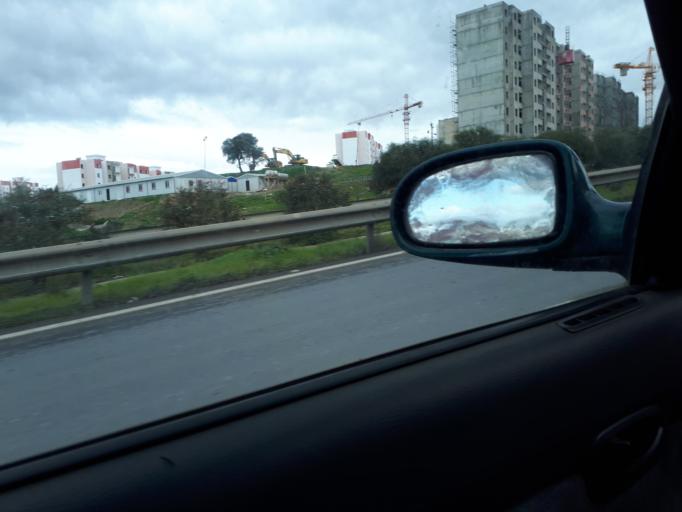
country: DZ
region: Tipaza
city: Douera
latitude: 36.7067
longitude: 2.9329
